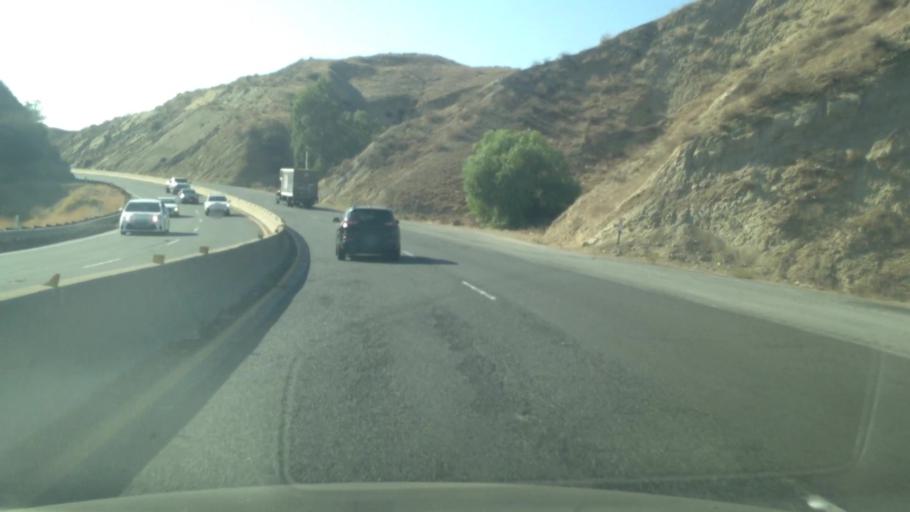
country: US
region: California
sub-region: Riverside County
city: Calimesa
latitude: 33.9372
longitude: -117.1037
